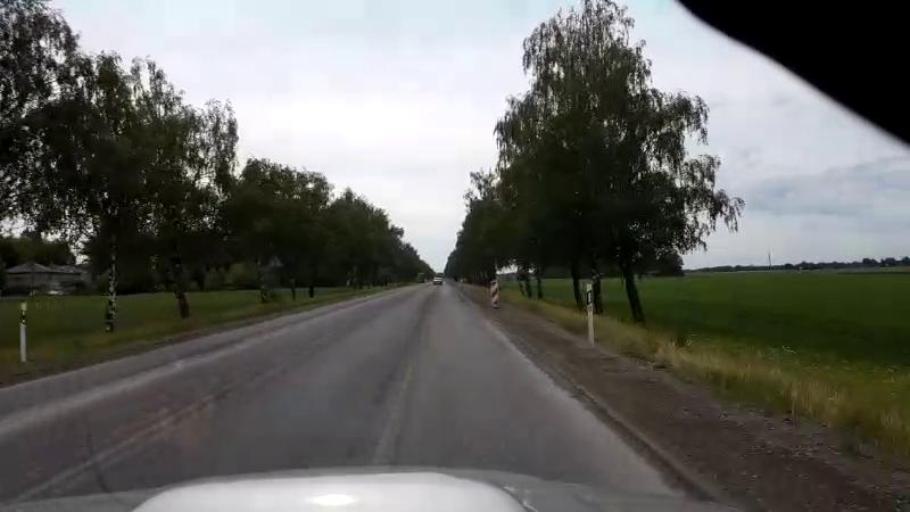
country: LV
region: Bauskas Rajons
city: Bauska
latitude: 56.3559
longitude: 24.2851
